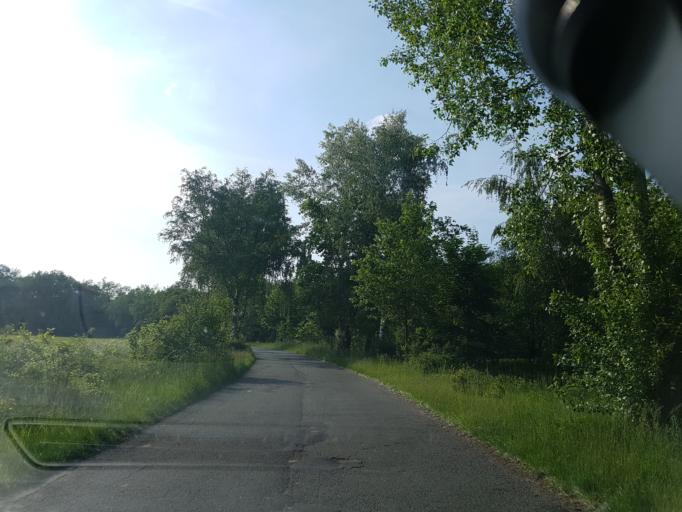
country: PL
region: Lower Silesian Voivodeship
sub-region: Powiat strzelinski
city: Wiazow
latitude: 50.8444
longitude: 17.2517
